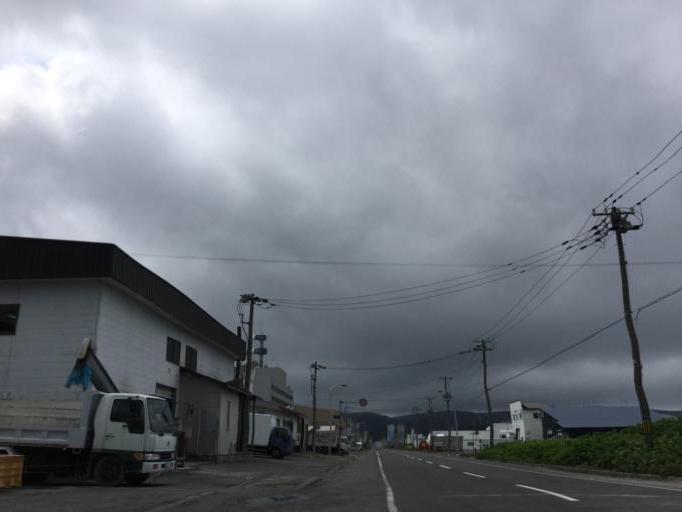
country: JP
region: Hokkaido
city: Wakkanai
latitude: 45.4003
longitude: 141.7056
